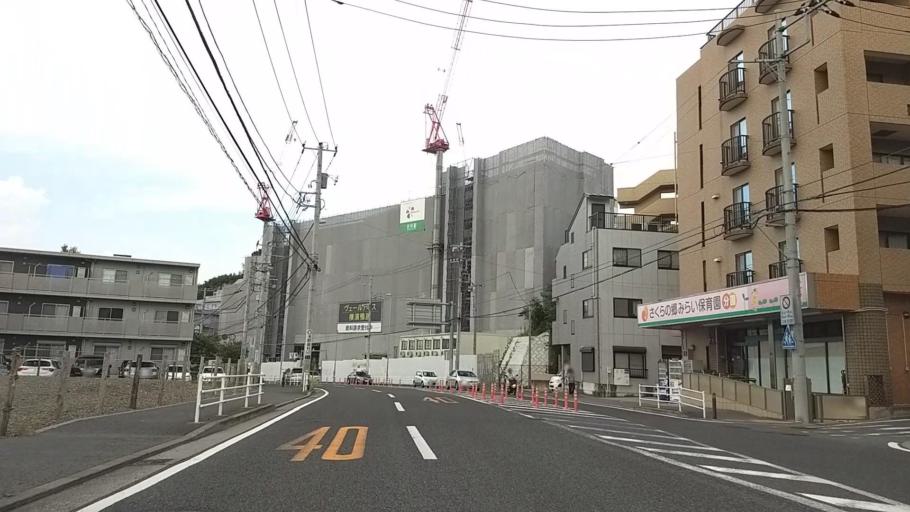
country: JP
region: Kanagawa
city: Yokohama
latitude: 35.5052
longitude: 139.5638
